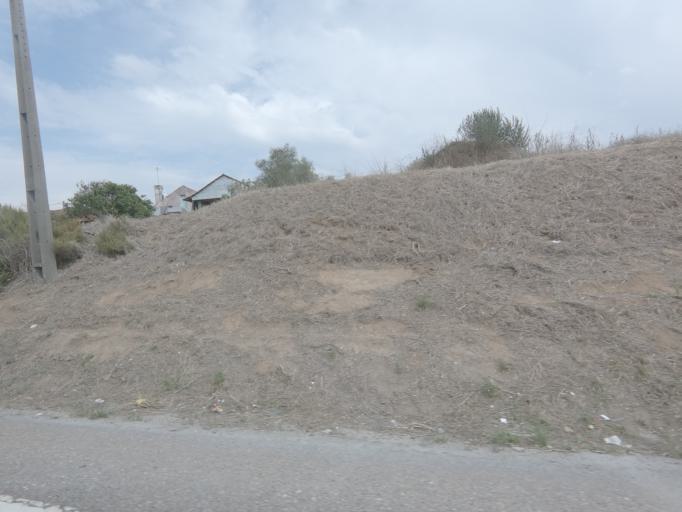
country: PT
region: Leiria
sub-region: Leiria
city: Caranguejeira
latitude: 39.8224
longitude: -8.7270
